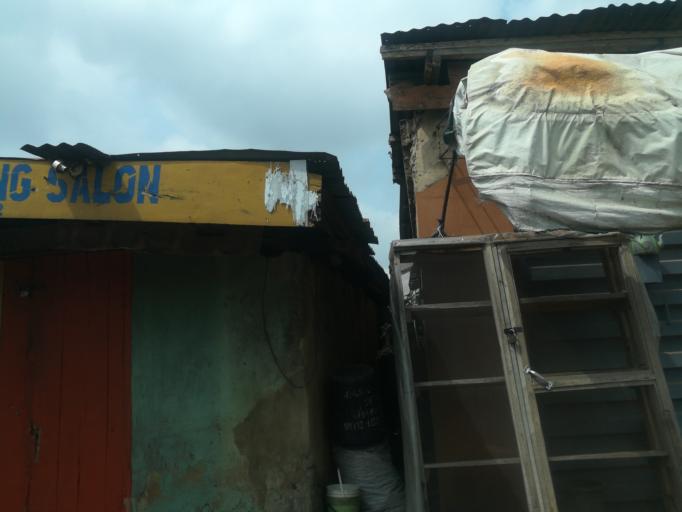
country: NG
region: Oyo
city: Ibadan
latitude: 7.4136
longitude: 3.9519
